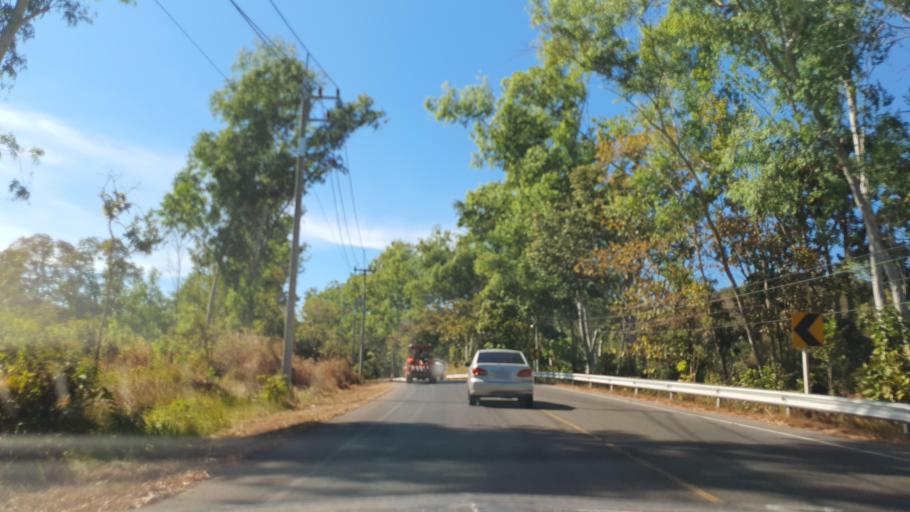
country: TH
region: Kalasin
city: Khao Wong
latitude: 16.7656
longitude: 104.1384
